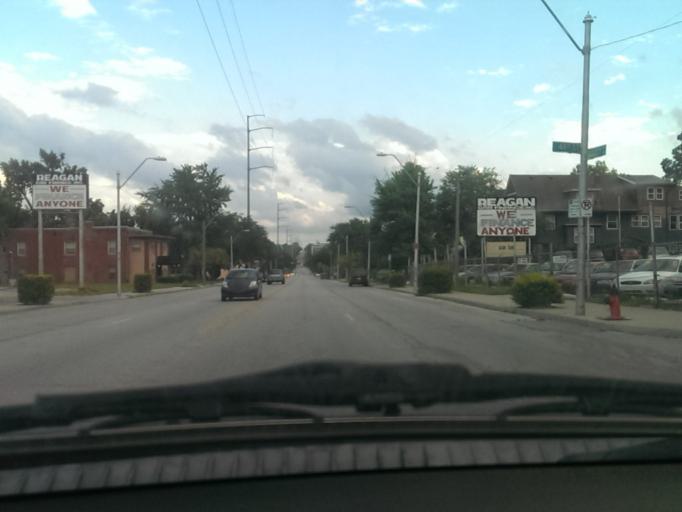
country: US
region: Kansas
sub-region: Johnson County
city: Westwood
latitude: 39.0472
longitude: -94.5726
